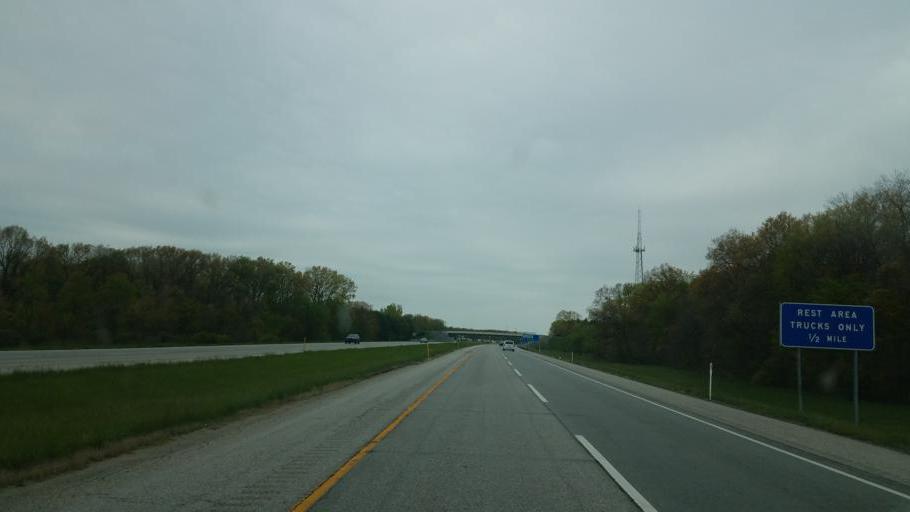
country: US
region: Michigan
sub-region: Saint Joseph County
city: White Pigeon
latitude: 41.7520
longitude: -85.6546
